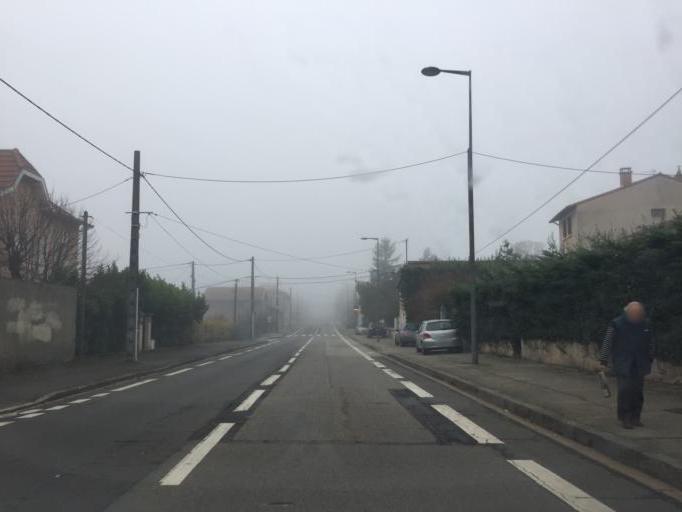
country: FR
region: Rhone-Alpes
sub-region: Departement du Rhone
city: Sathonay-Camp
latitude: 45.8018
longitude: 4.8678
